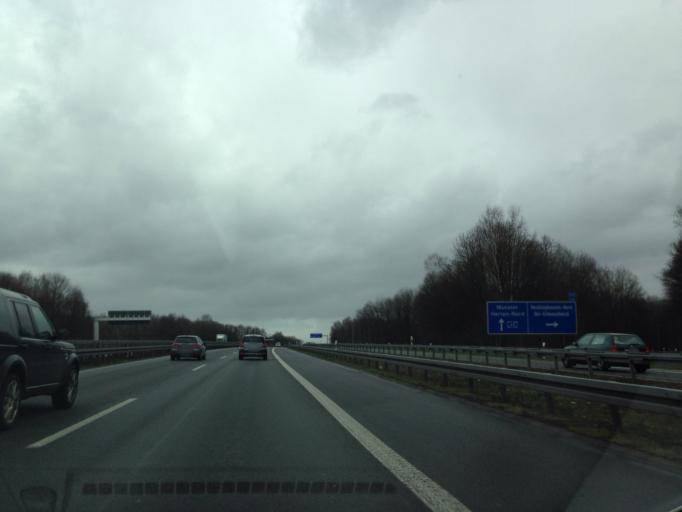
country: DE
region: North Rhine-Westphalia
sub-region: Regierungsbezirk Munster
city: Recklinghausen
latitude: 51.6179
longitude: 7.1685
